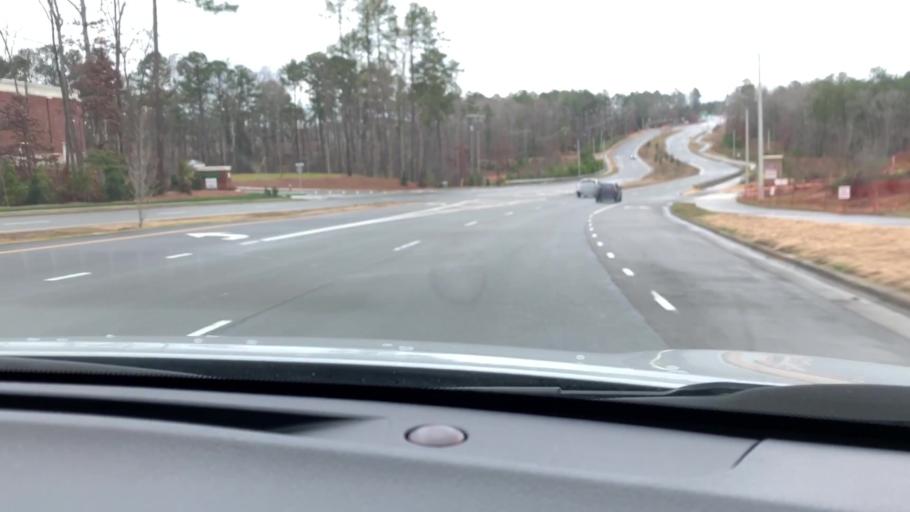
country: US
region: North Carolina
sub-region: Wake County
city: Green Level
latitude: 35.8247
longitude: -78.9022
